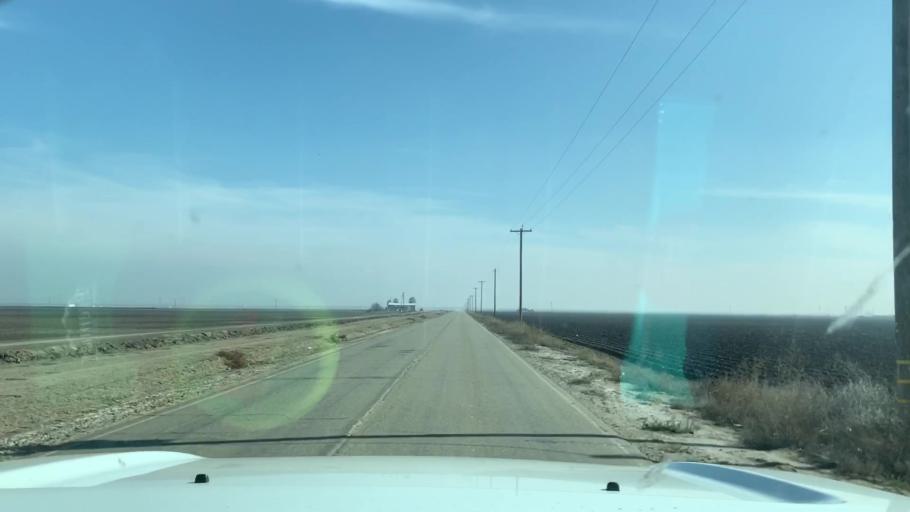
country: US
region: California
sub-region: Kern County
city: Buttonwillow
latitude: 35.4420
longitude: -119.5265
